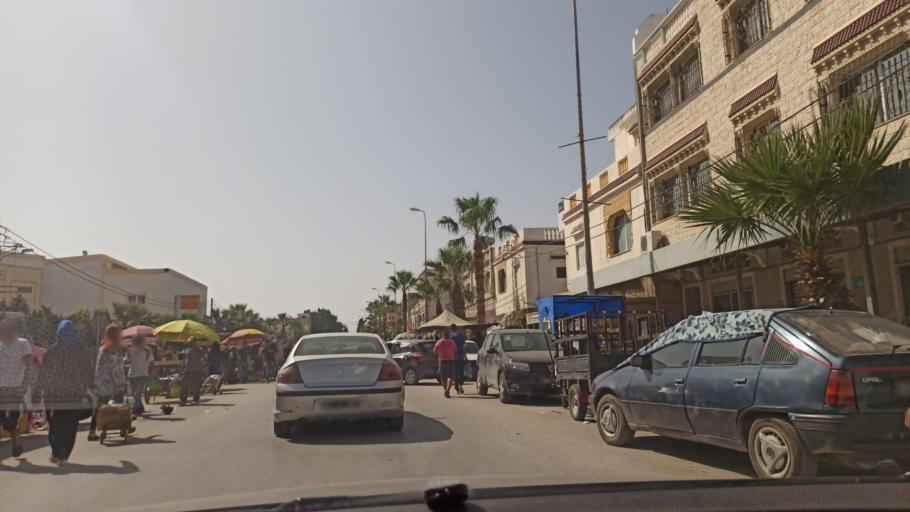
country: TN
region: Manouba
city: Manouba
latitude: 36.7694
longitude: 10.1122
